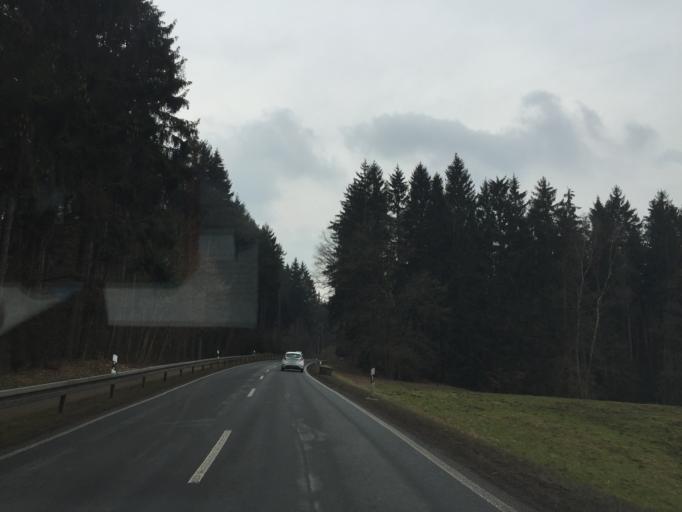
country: DE
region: Thuringia
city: Kranichfeld
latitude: 50.8686
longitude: 11.1998
